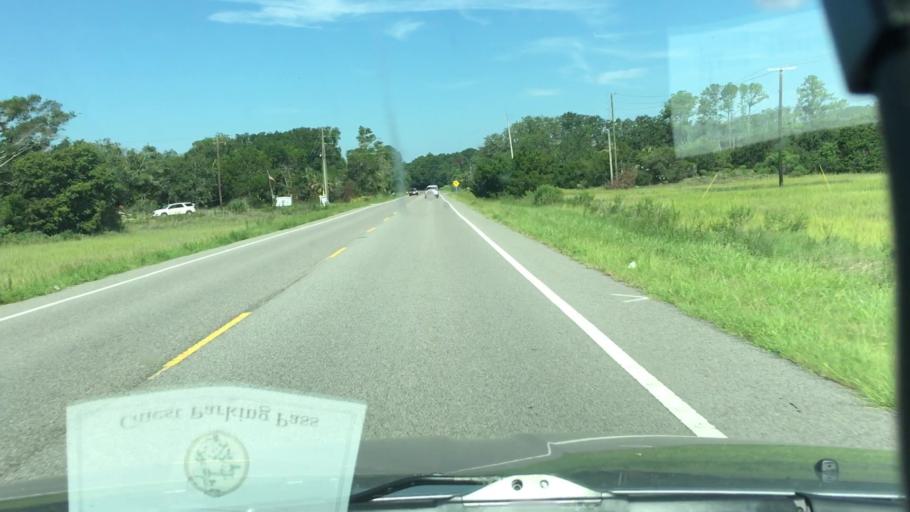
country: US
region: South Carolina
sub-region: Beaufort County
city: Beaufort
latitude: 32.4127
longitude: -80.4770
